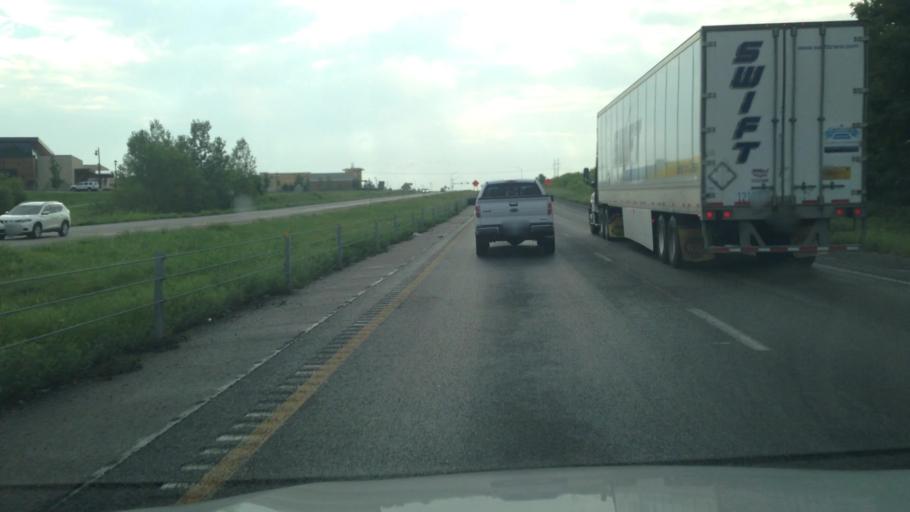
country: US
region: Missouri
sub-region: Clay County
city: Pleasant Valley
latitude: 39.2450
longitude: -94.4691
